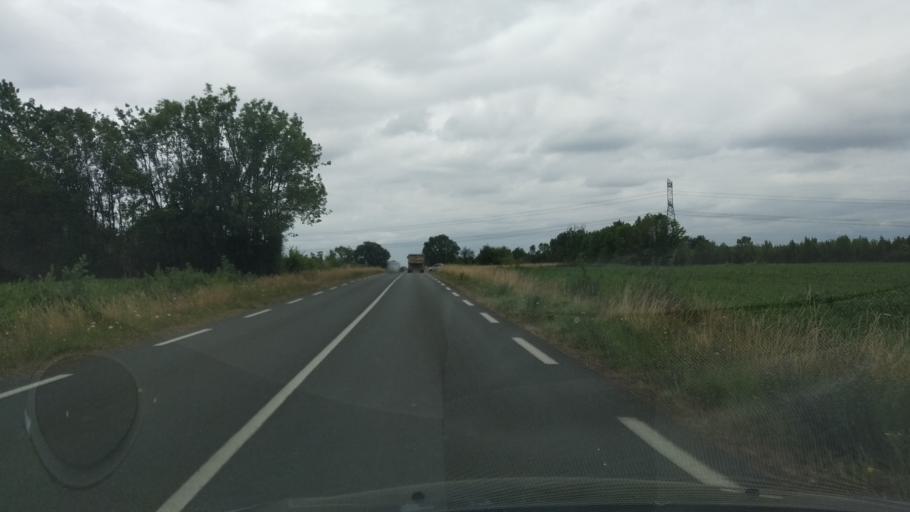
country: FR
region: Poitou-Charentes
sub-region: Departement de la Vienne
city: Saint-Maurice-la-Clouere
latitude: 46.3925
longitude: 0.3996
